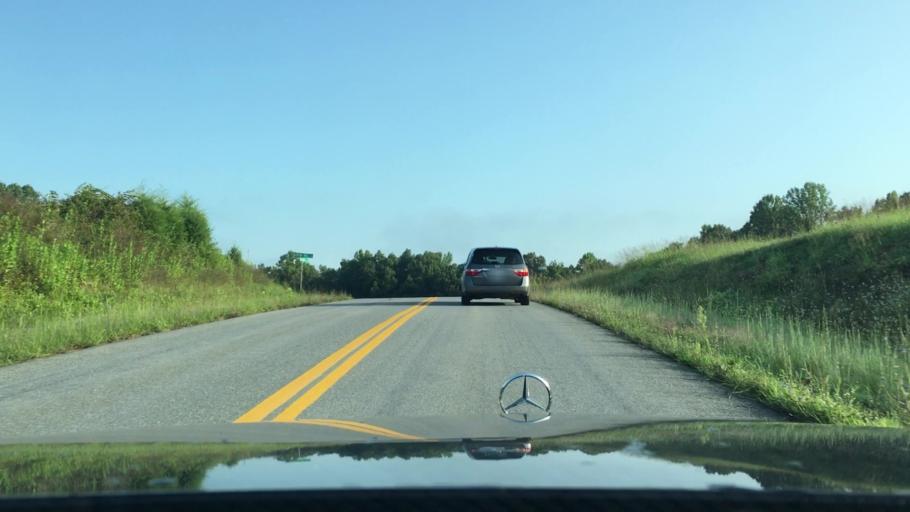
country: US
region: Virginia
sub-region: Campbell County
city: Timberlake
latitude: 37.2871
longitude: -79.2722
